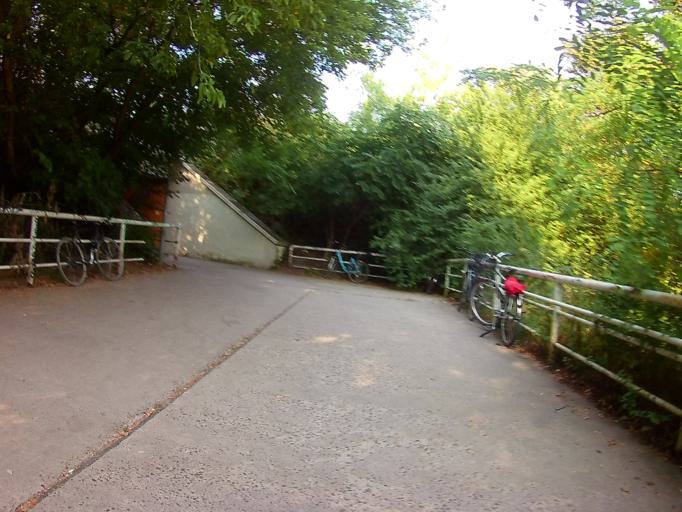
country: DE
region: Berlin
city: Kaulsdorf
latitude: 52.5121
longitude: 13.5741
